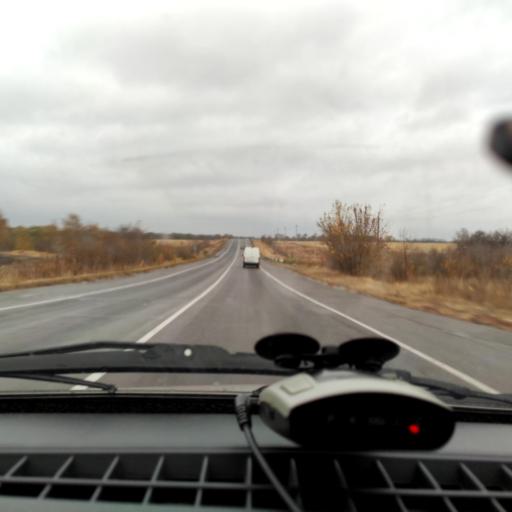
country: RU
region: Voronezj
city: Devitsa
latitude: 51.5718
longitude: 38.9748
